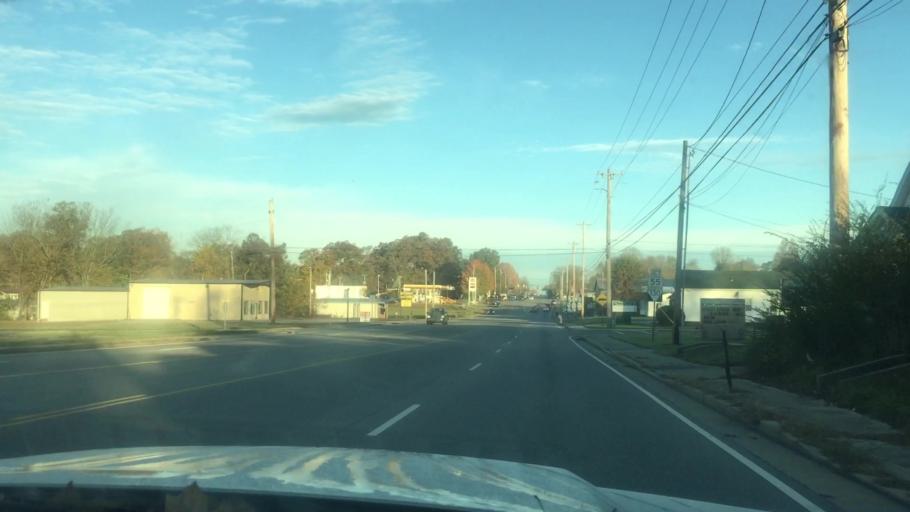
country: US
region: Tennessee
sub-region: Coffee County
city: Tullahoma
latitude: 35.3535
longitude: -86.2040
